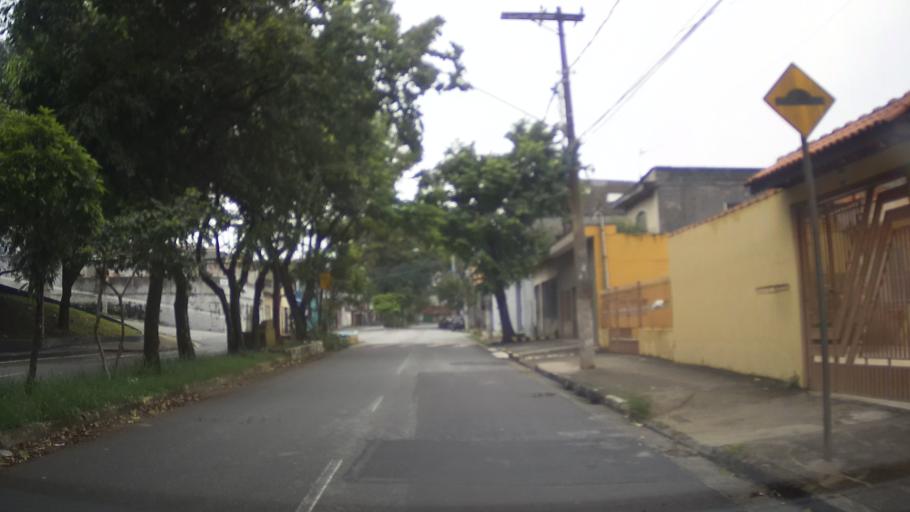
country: BR
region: Sao Paulo
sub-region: Guarulhos
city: Guarulhos
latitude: -23.5009
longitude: -46.5583
